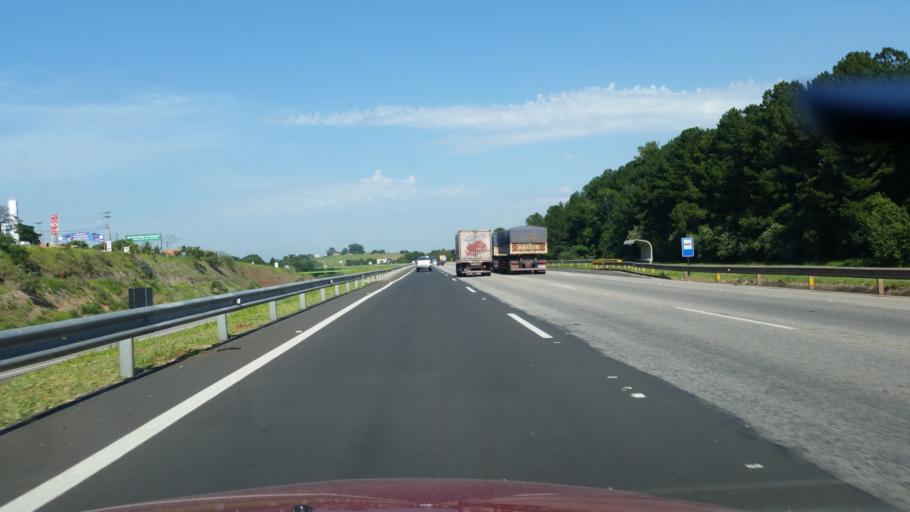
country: BR
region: Sao Paulo
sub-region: Boituva
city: Boituva
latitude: -23.2957
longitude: -47.6853
